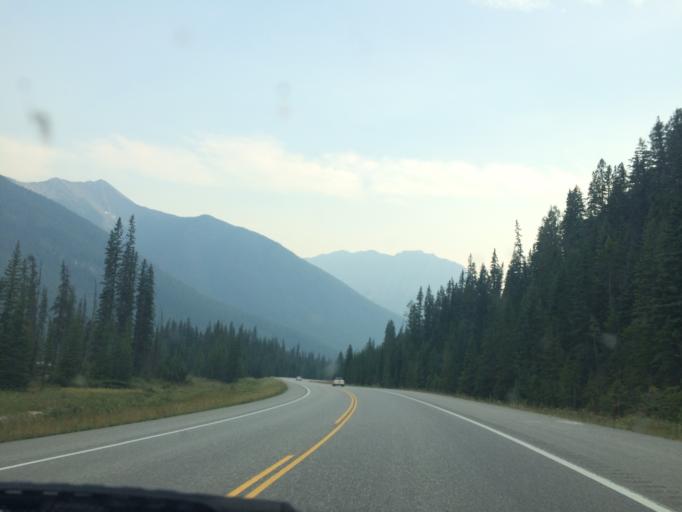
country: CA
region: Alberta
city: Banff
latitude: 50.9661
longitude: -115.9531
